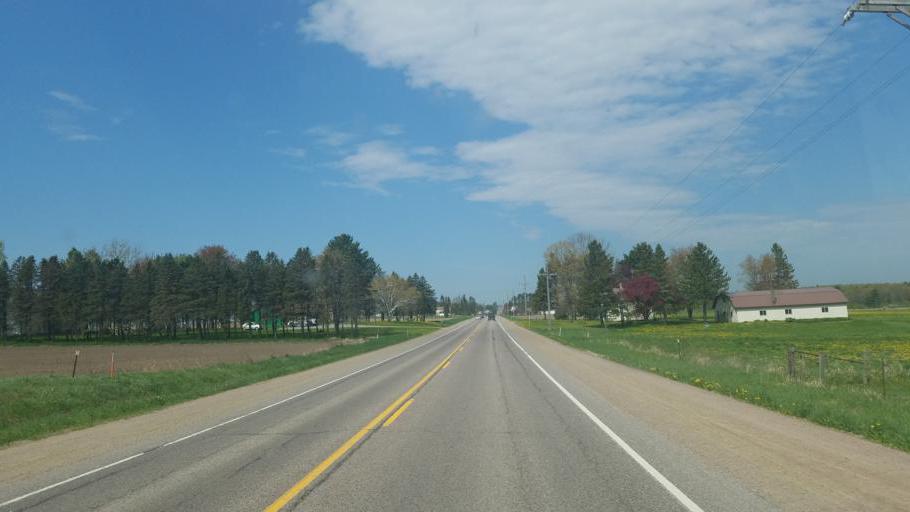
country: US
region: Wisconsin
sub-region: Clark County
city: Loyal
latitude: 44.5829
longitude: -90.3857
